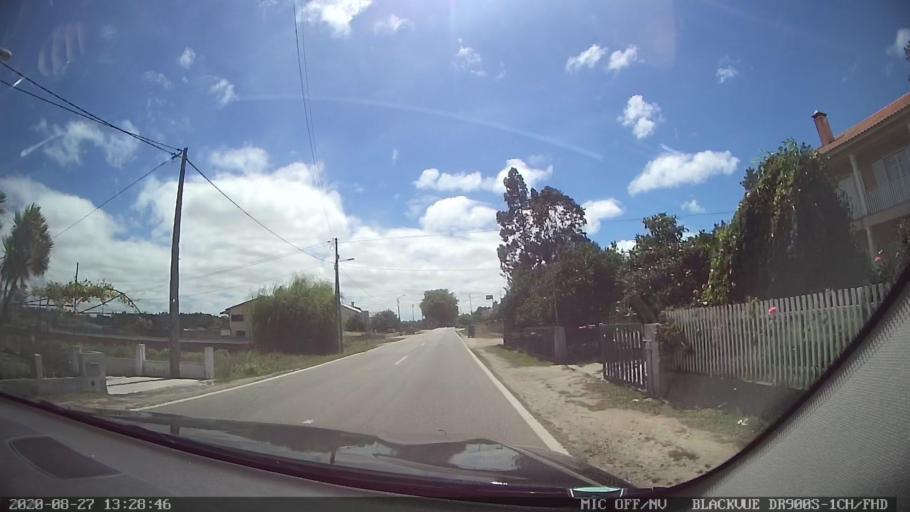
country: PT
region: Aveiro
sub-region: Vagos
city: Vagos
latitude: 40.5165
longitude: -8.6784
